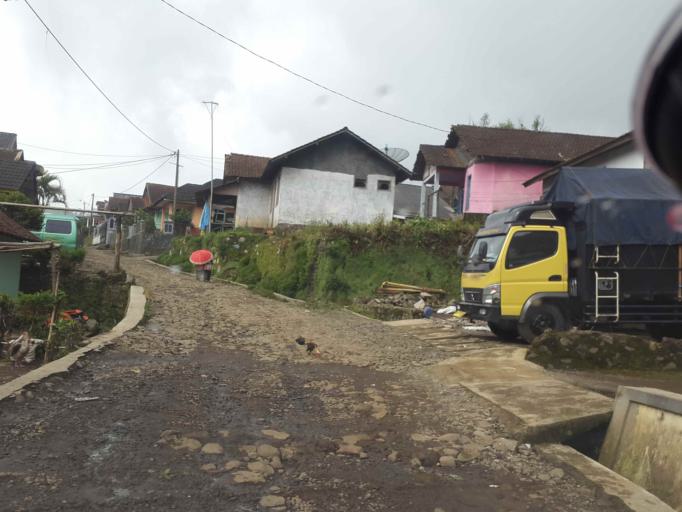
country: ID
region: Central Java
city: Baturaden
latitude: -7.2733
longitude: 109.1128
